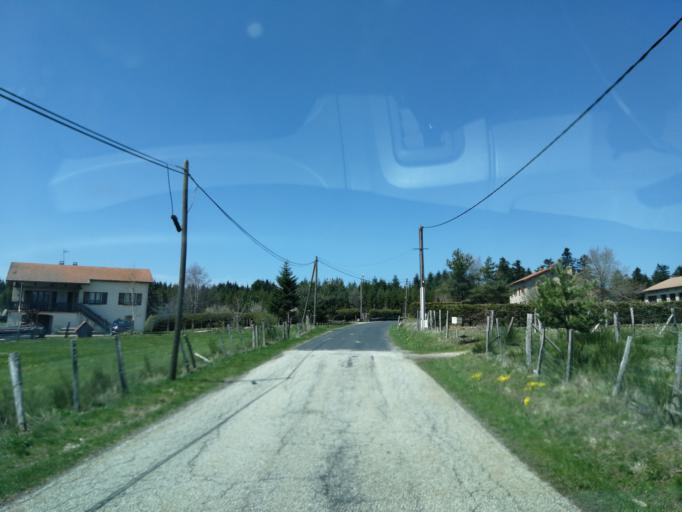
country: FR
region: Auvergne
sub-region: Departement de la Haute-Loire
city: Riotord
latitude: 45.1220
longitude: 4.4062
